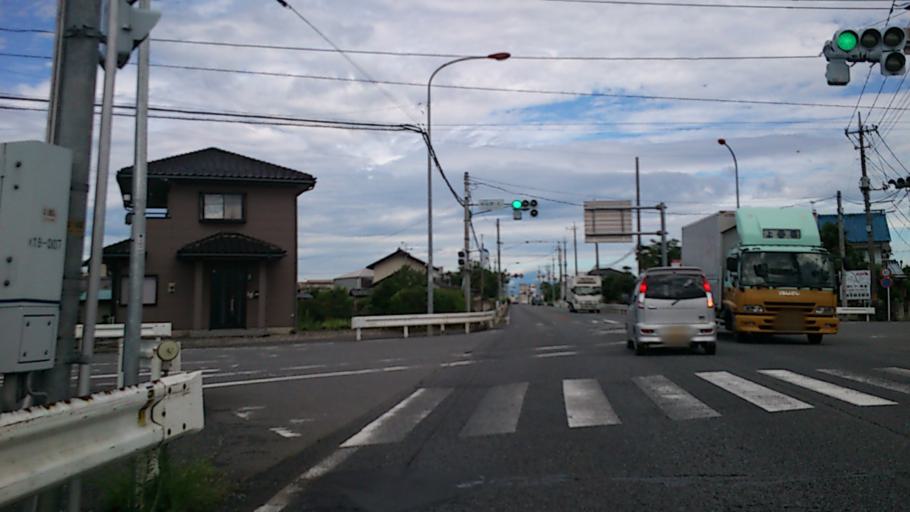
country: JP
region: Saitama
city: Honjo
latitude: 36.2600
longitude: 139.1474
